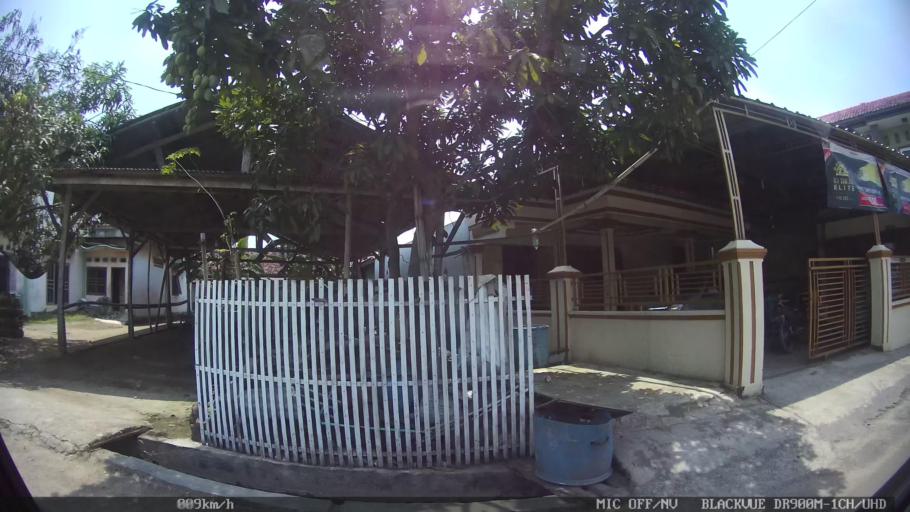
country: ID
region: Lampung
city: Bandarlampung
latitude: -5.4577
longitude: 105.2618
